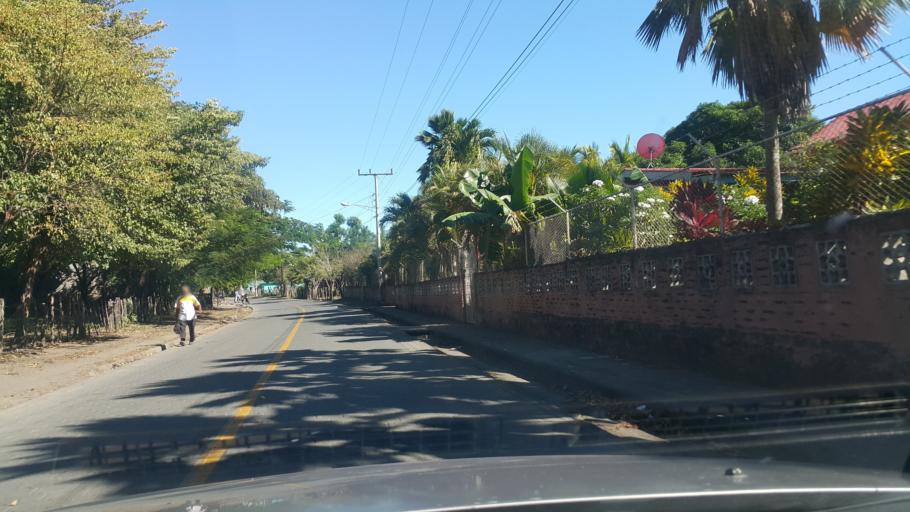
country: NI
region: Rivas
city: Moyogalpa
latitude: 11.4857
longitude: -85.6470
